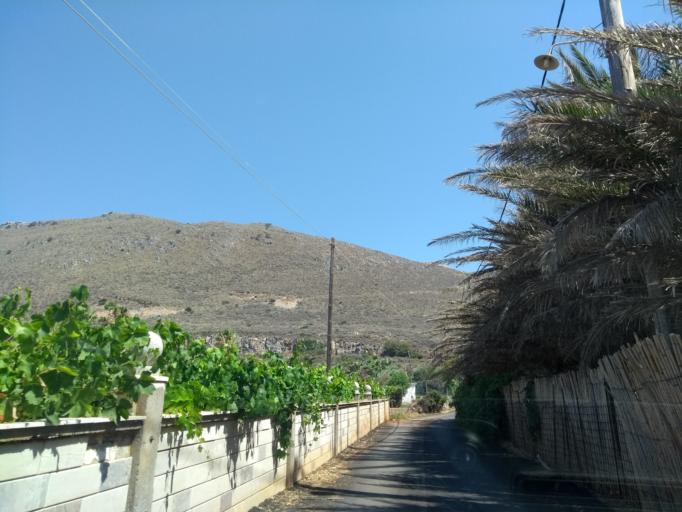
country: GR
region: Crete
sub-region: Nomos Rethymnis
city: Atsipopoulon
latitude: 35.3579
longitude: 24.3679
